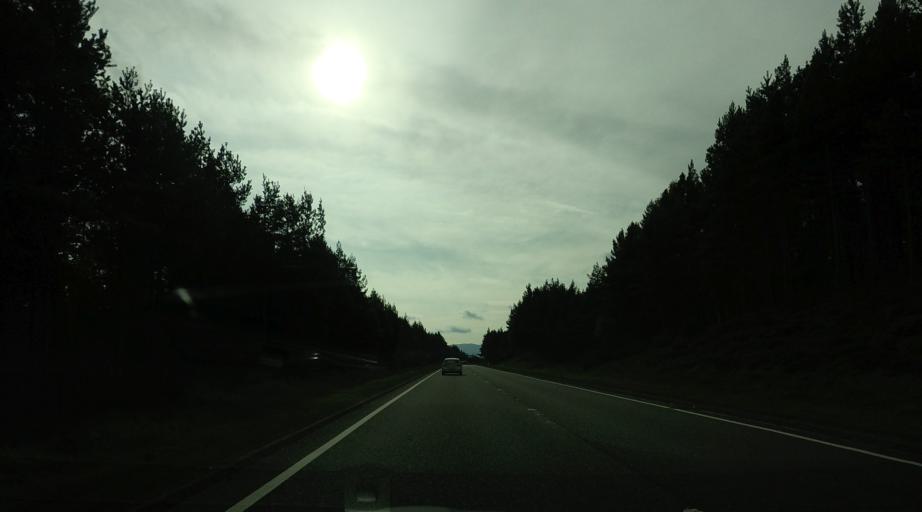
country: GB
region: Scotland
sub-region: Highland
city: Aviemore
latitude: 57.2597
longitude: -3.8102
